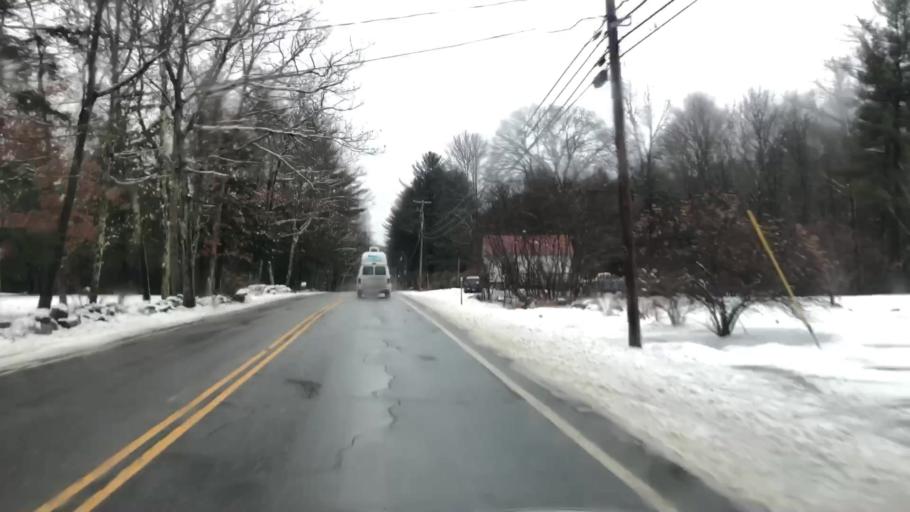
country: US
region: New Hampshire
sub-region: Hillsborough County
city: Weare
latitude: 43.0444
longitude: -71.7077
